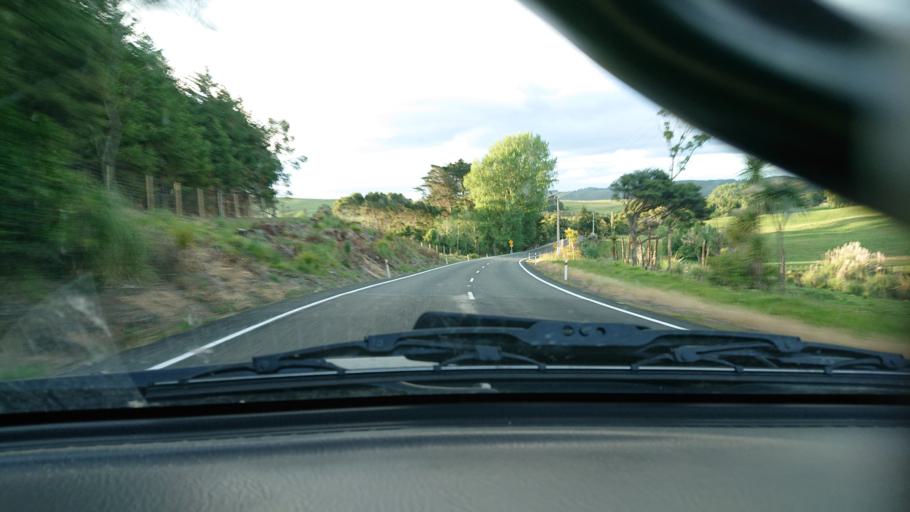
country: NZ
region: Auckland
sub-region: Auckland
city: Parakai
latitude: -36.5235
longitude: 174.4502
